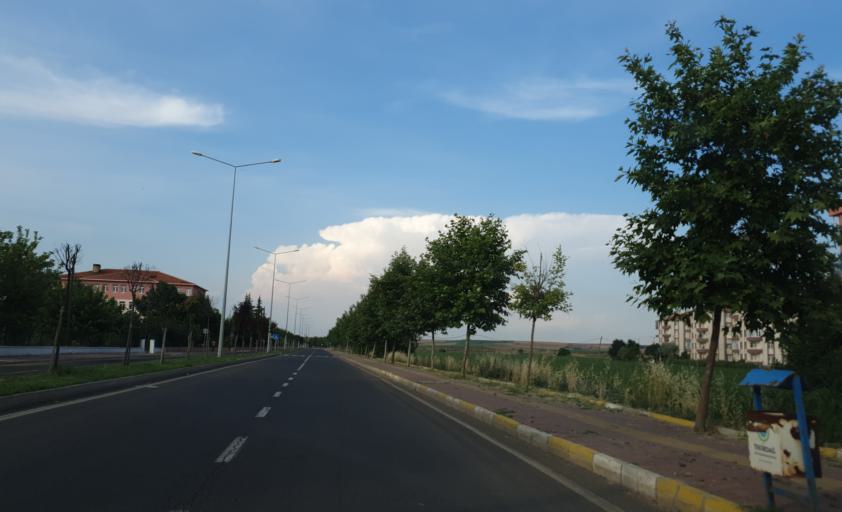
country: TR
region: Tekirdag
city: Hayrabolu
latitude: 41.2205
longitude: 27.1123
